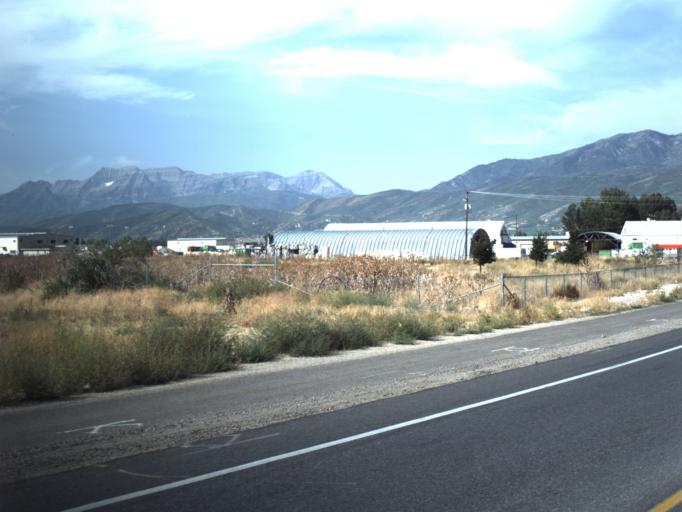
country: US
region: Utah
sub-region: Wasatch County
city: Heber
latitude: 40.5067
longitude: -111.4235
